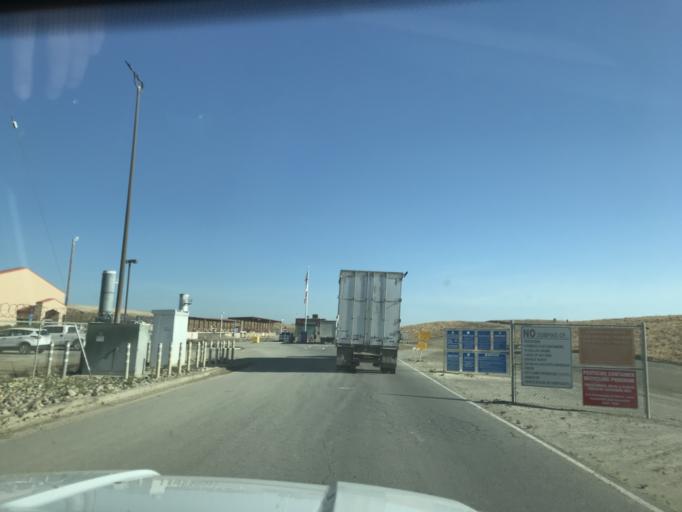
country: US
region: California
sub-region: Fresno County
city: San Joaquin
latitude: 36.6625
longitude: -120.1333
